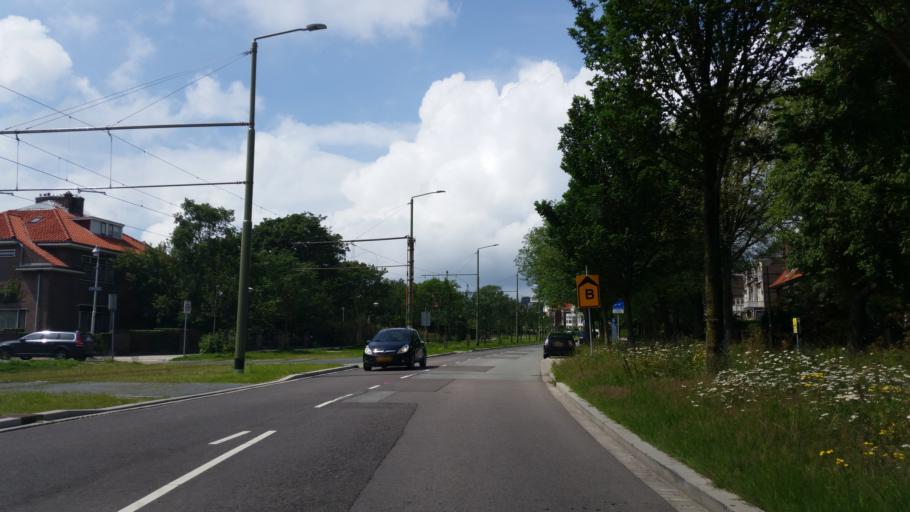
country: NL
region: South Holland
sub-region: Gemeente Den Haag
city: Scheveningen
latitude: 52.1079
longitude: 4.2888
